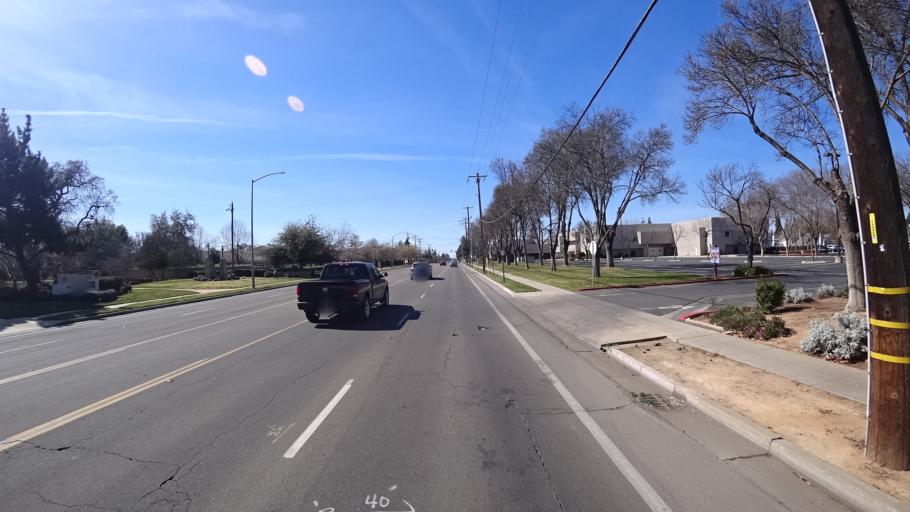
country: US
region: California
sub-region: Fresno County
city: Clovis
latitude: 36.8448
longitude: -119.7634
